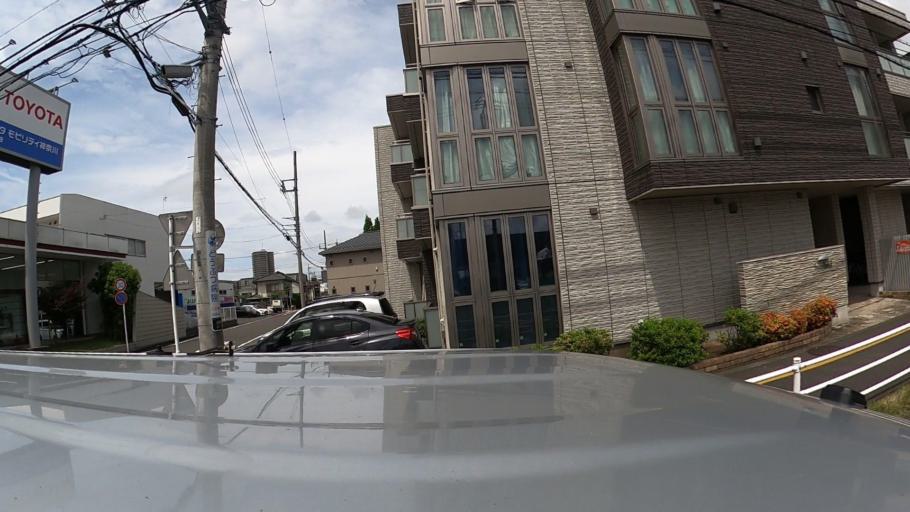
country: JP
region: Kanagawa
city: Fujisawa
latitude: 35.4010
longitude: 139.4695
